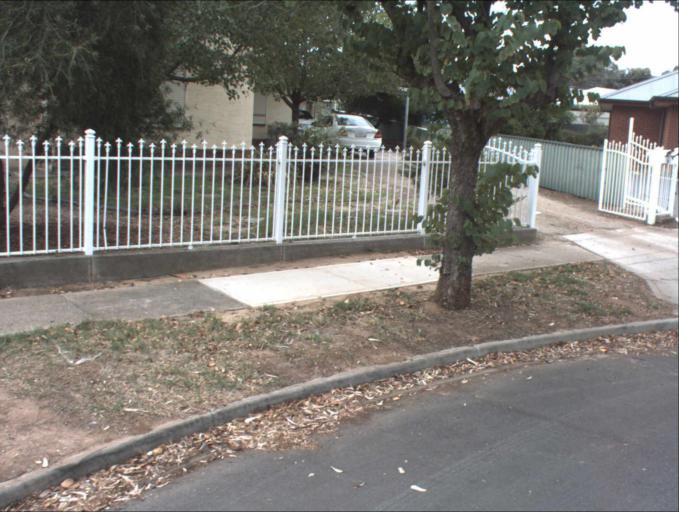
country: AU
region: South Australia
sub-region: Port Adelaide Enfield
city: Enfield
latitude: -34.8562
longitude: 138.6220
